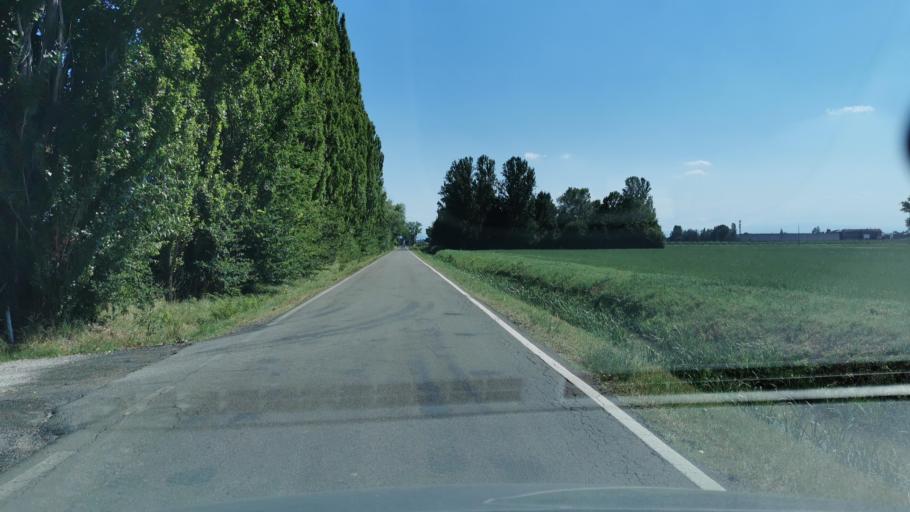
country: IT
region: Emilia-Romagna
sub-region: Provincia di Modena
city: Limidi
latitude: 44.7755
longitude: 10.9179
